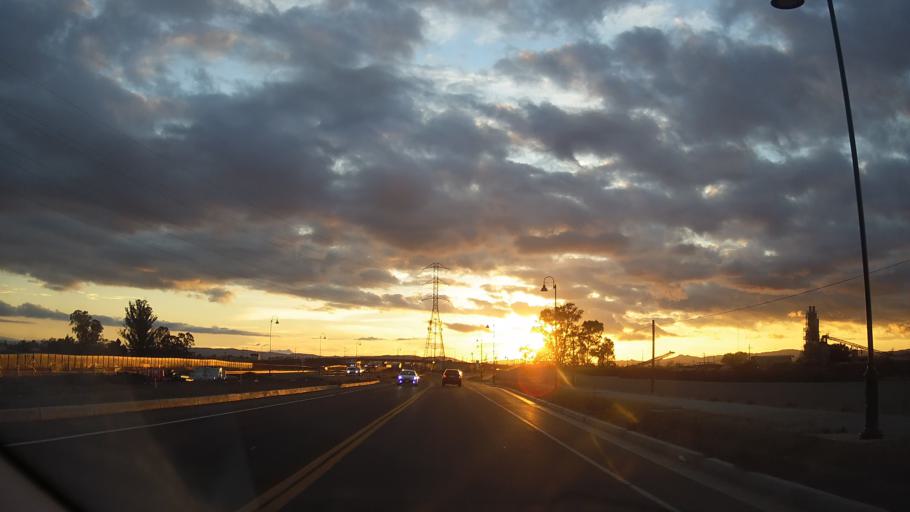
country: US
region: California
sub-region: Solano County
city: Vacaville
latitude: 38.2886
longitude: -121.9633
